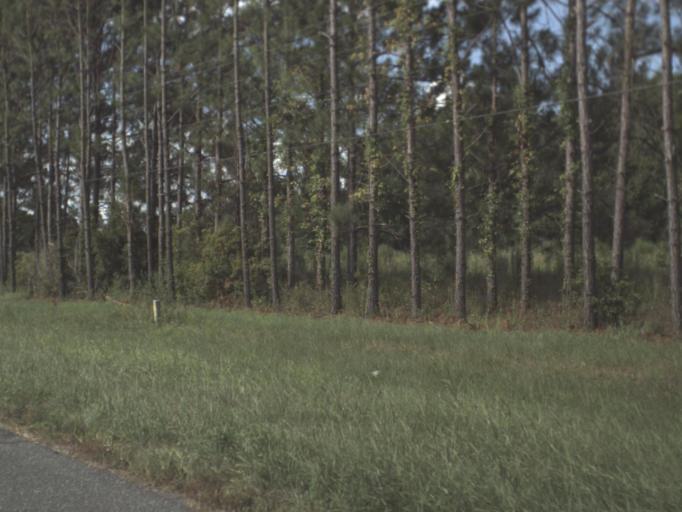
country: US
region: Florida
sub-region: Taylor County
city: Perry
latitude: 30.2466
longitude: -83.6214
